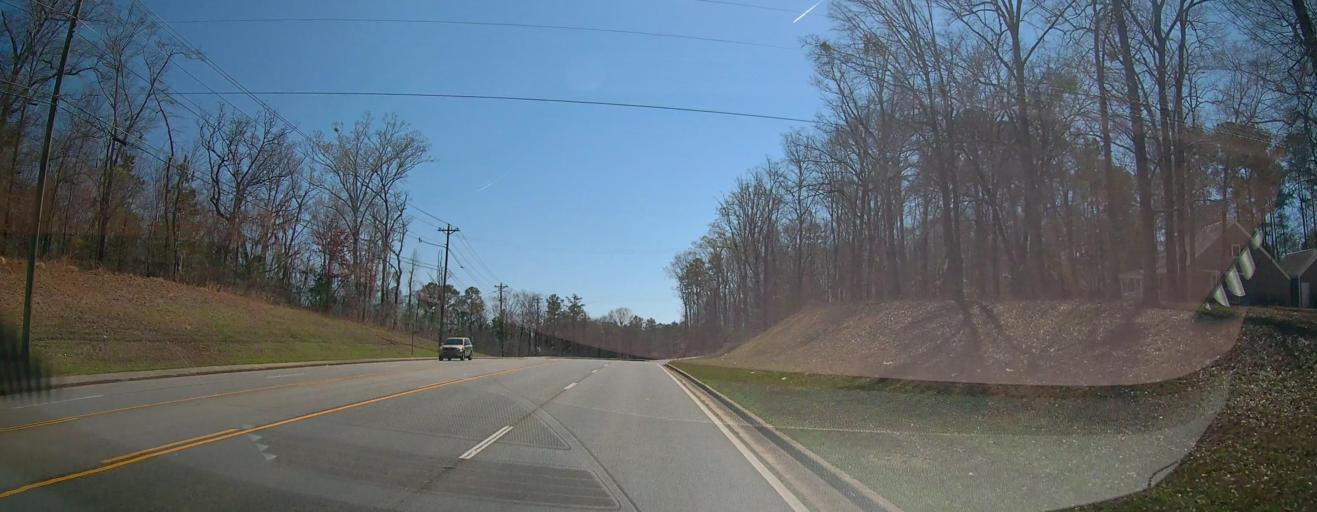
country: US
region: Georgia
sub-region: Houston County
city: Robins Air Force Base
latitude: 32.5431
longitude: -83.6250
